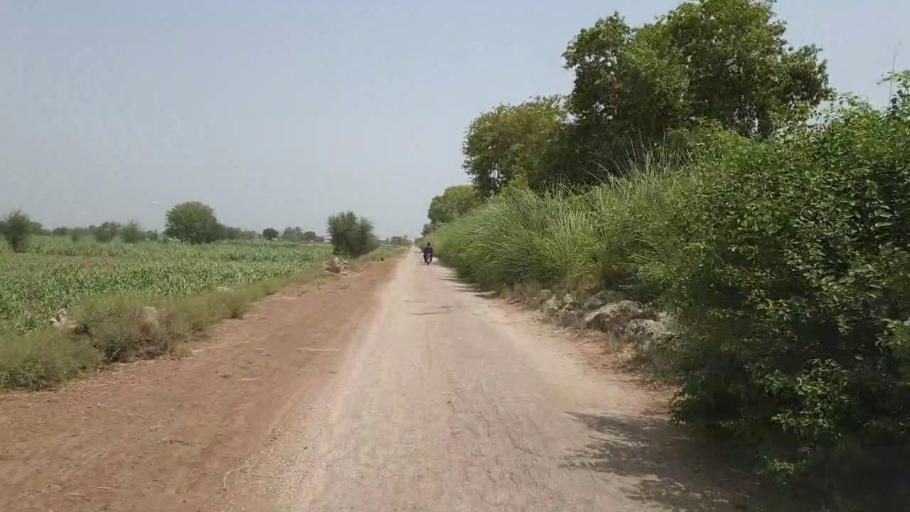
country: PK
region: Sindh
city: Nawabshah
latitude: 26.2971
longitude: 68.3063
